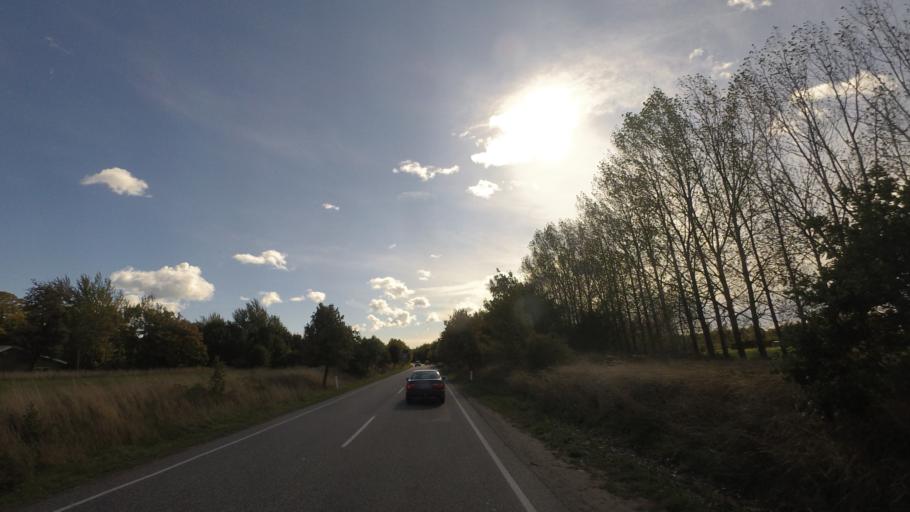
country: DK
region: Capital Region
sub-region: Bornholm Kommune
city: Ronne
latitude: 55.0916
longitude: 14.7280
